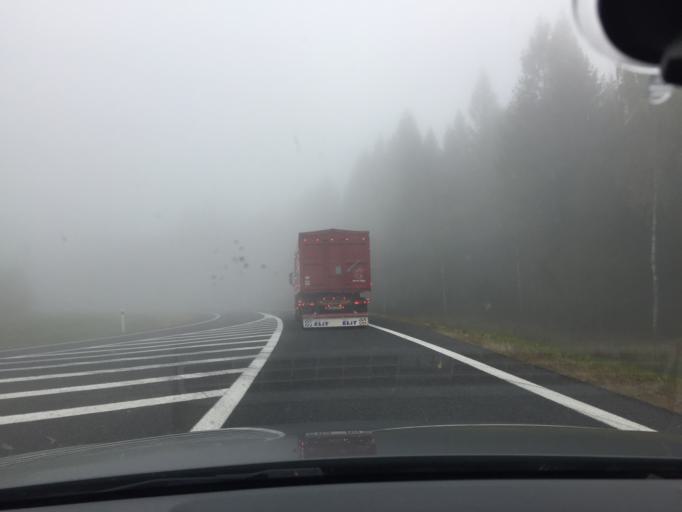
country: CZ
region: Ustecky
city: Chlumec
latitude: 50.7673
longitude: 13.9653
